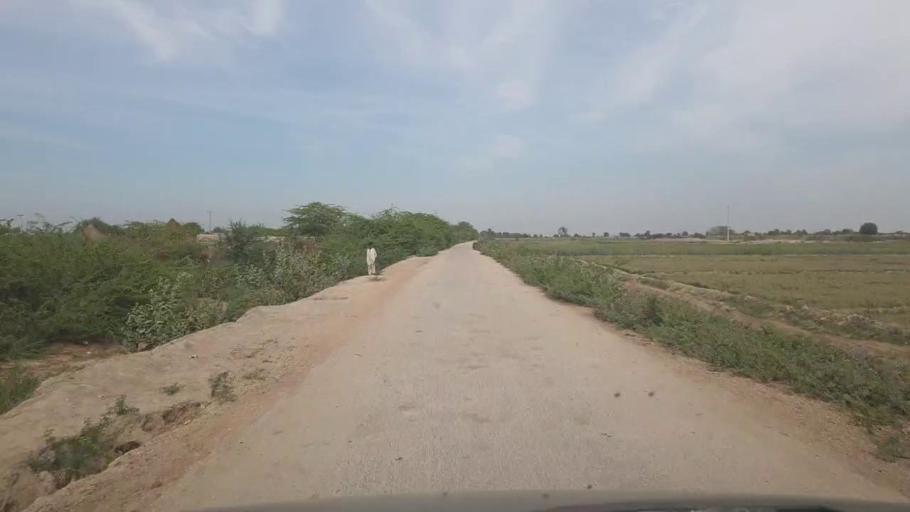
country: PK
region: Sindh
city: Kunri
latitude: 25.2530
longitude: 69.6264
